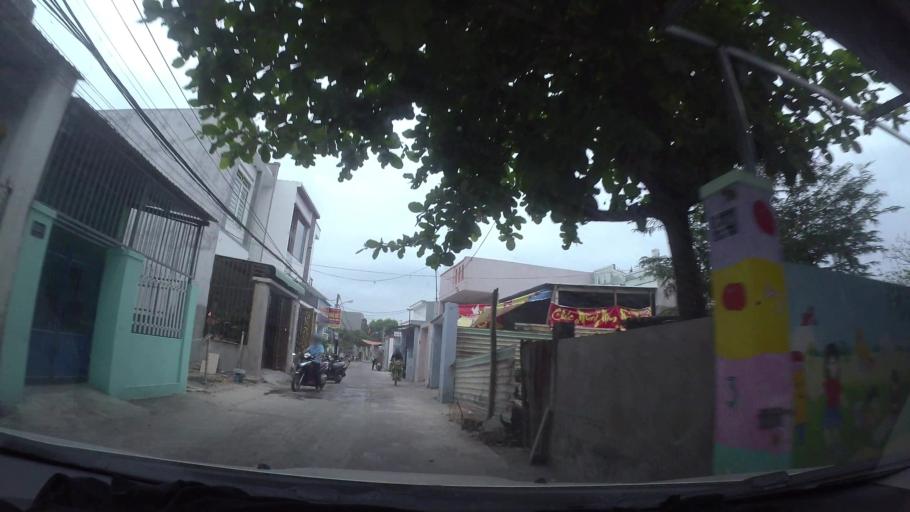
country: VN
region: Da Nang
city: Lien Chieu
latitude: 16.0839
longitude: 108.1553
